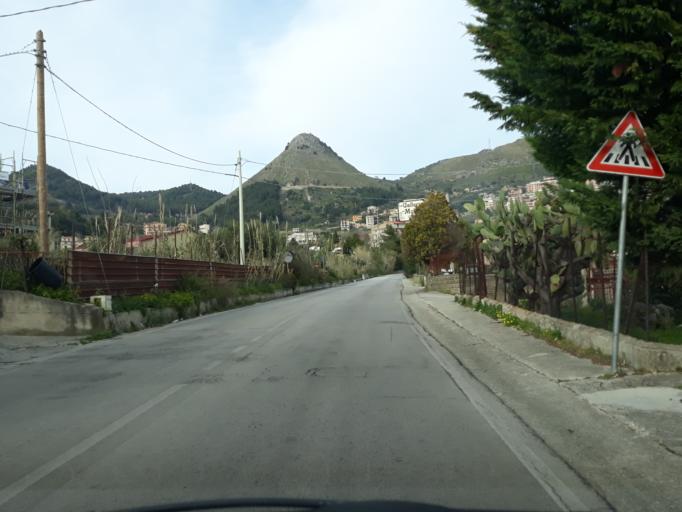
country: IT
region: Sicily
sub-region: Palermo
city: Giardinello
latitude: 38.0847
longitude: 13.1635
